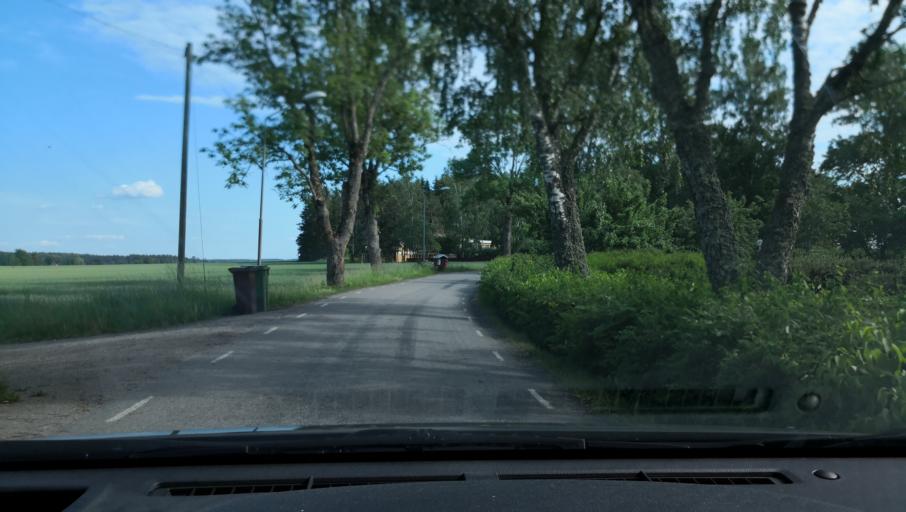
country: SE
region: Uppsala
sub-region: Enkopings Kommun
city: Irsta
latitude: 59.7656
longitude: 16.9871
